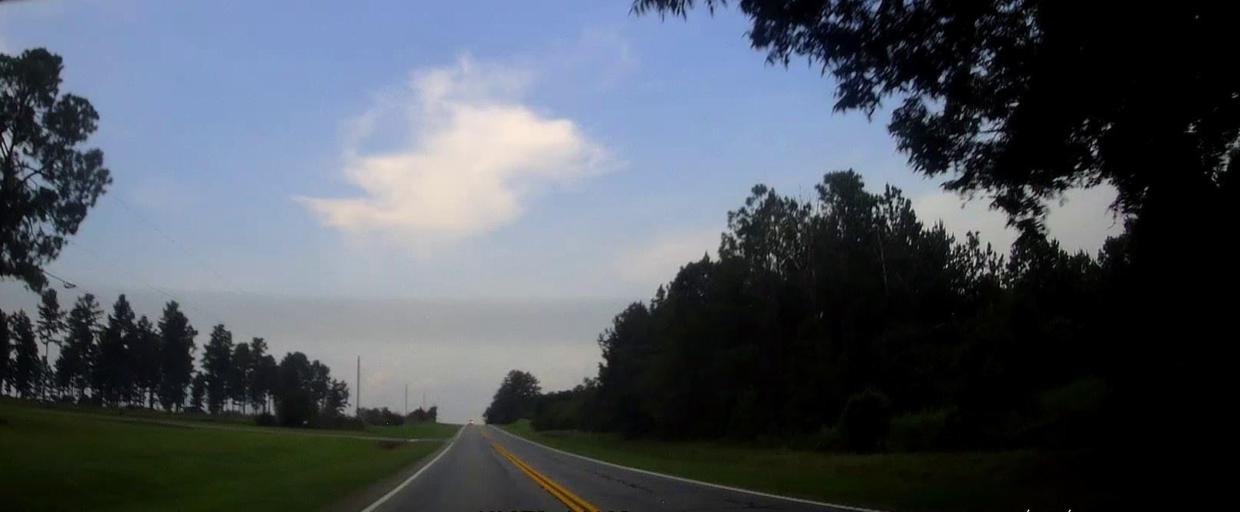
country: US
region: Georgia
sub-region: Laurens County
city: East Dublin
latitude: 32.5865
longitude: -82.8331
